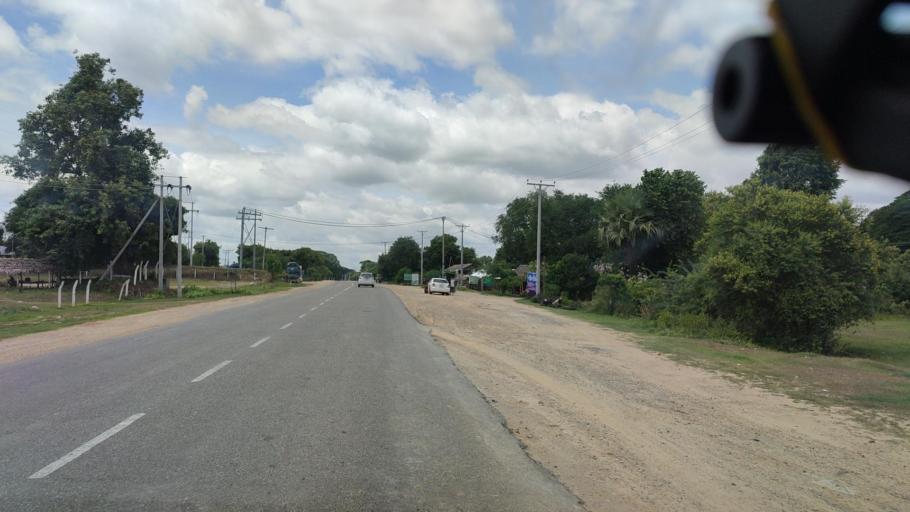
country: MM
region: Mandalay
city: Meiktila
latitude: 20.7976
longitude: 95.9125
